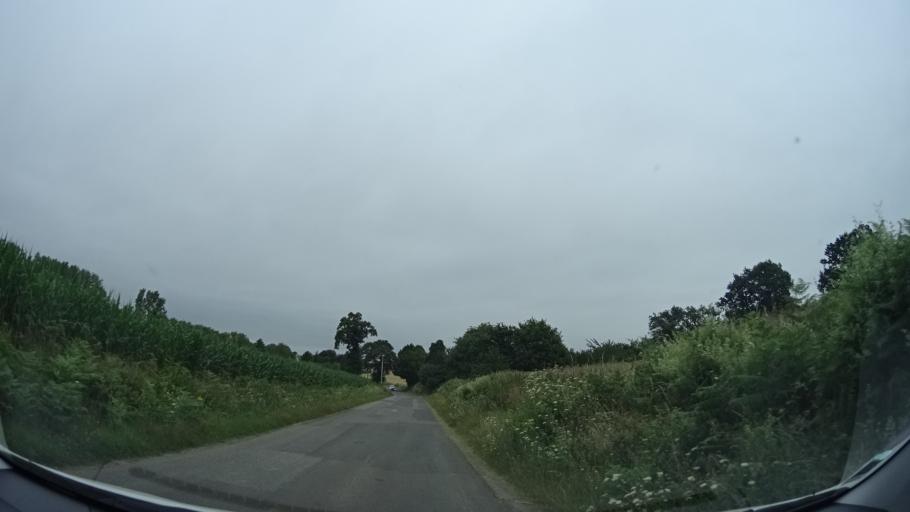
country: FR
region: Brittany
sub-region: Departement d'Ille-et-Vilaine
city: Irodouer
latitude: 48.3066
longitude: -1.9420
